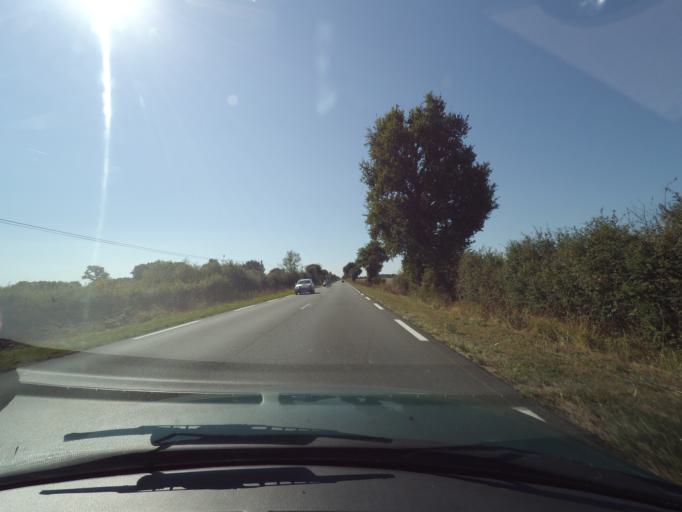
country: FR
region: Poitou-Charentes
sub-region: Departement de la Vienne
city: Saulge
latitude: 46.3140
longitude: 0.8266
